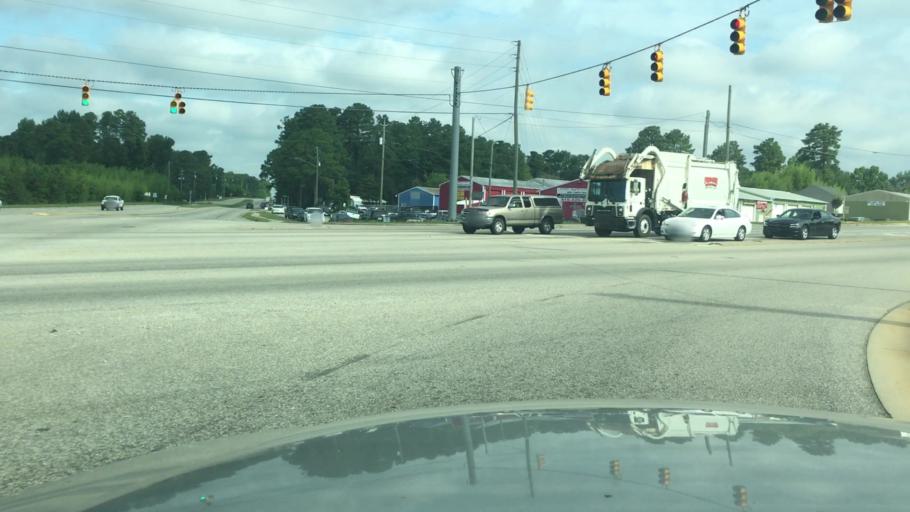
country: US
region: North Carolina
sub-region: Cumberland County
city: Hope Mills
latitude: 34.9956
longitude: -78.9675
